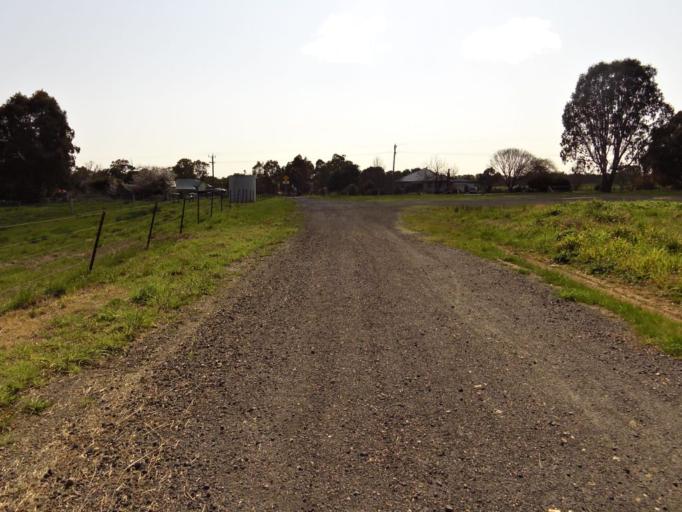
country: AU
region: Victoria
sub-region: Murrindindi
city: Alexandra
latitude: -37.1021
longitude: 145.6183
